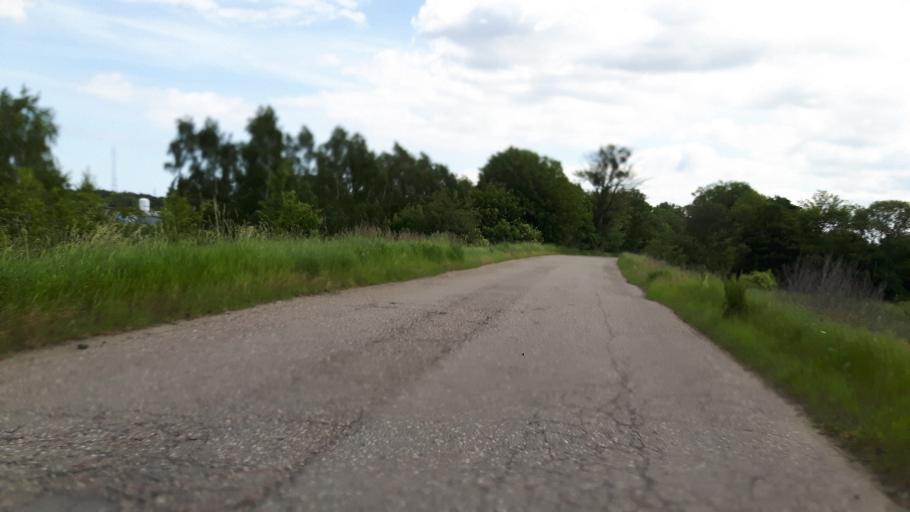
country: PL
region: Pomeranian Voivodeship
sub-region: Powiat gdanski
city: Cedry Wielkie
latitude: 54.3468
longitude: 18.7811
